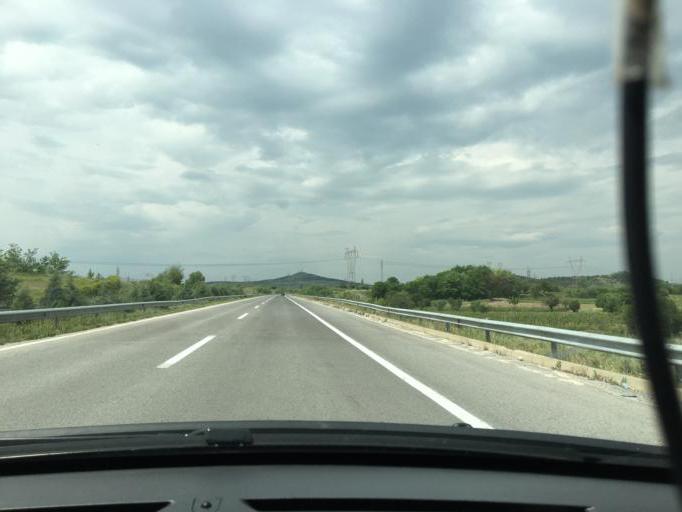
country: MK
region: Negotino
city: Negotino
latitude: 41.4548
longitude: 22.1525
